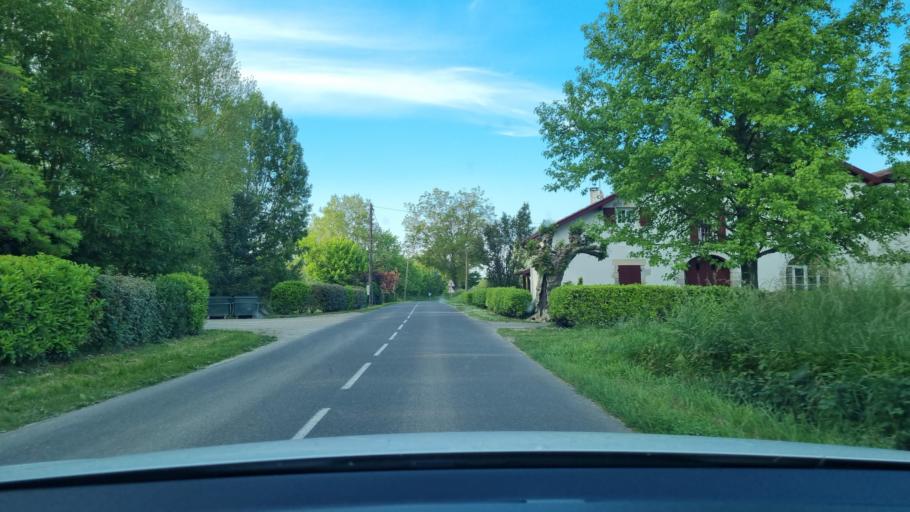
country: FR
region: Aquitaine
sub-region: Departement des Landes
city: Peyrehorade
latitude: 43.5396
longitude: -1.1423
